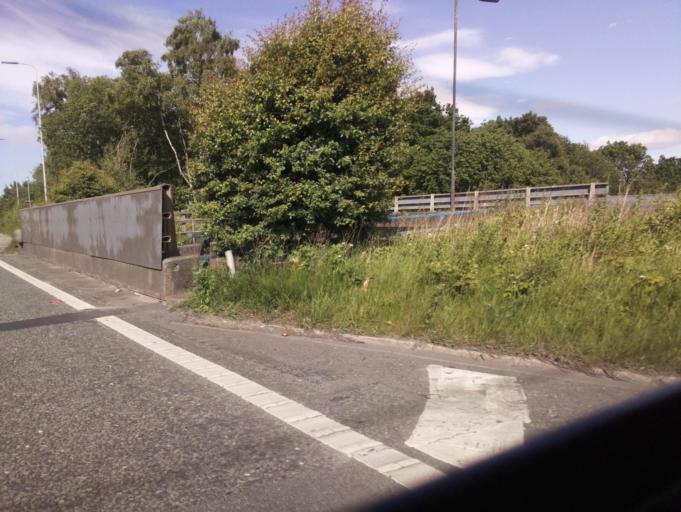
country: GB
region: England
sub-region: Borough of Bolton
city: Kearsley
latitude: 53.5193
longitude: -2.3671
